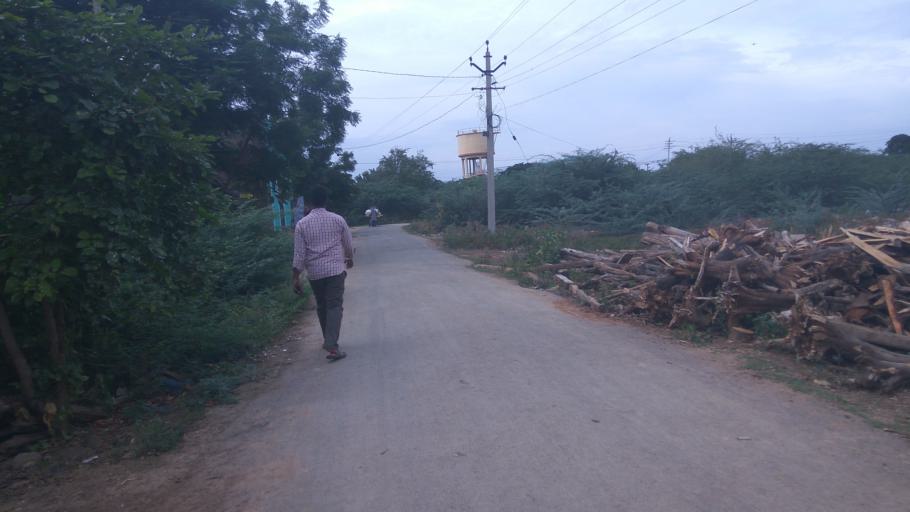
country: IN
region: Andhra Pradesh
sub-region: Prakasam
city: Cumbum
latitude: 15.5912
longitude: 79.1113
